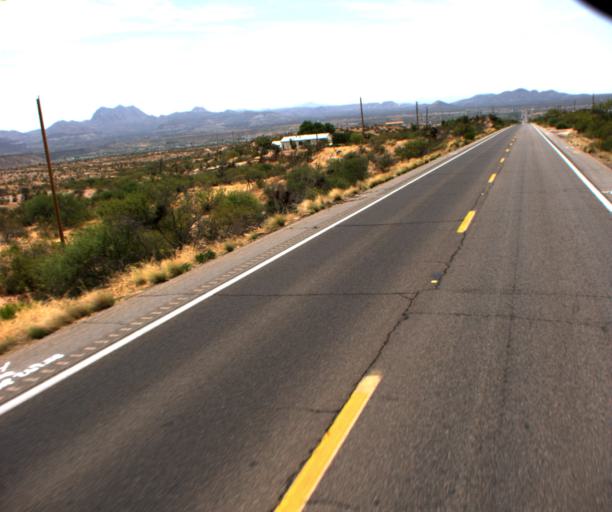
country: US
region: Arizona
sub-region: Gila County
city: Peridot
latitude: 33.3052
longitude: -110.4847
